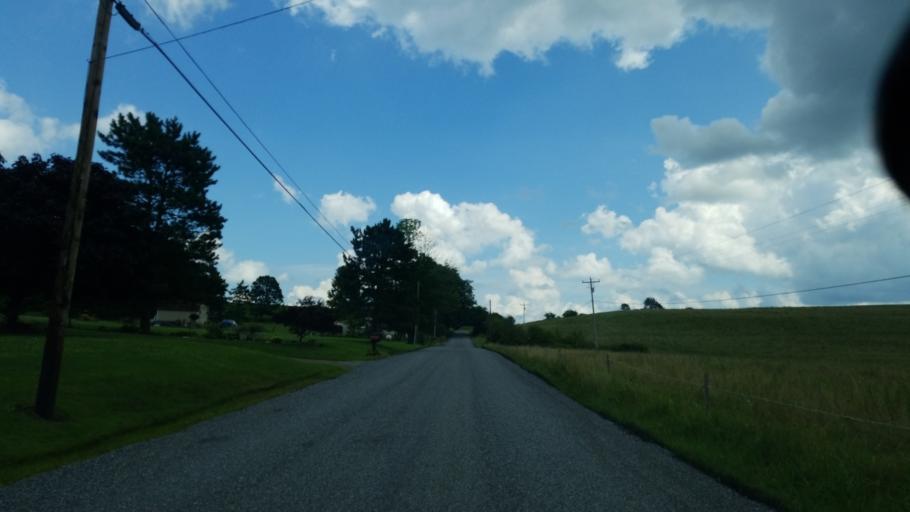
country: US
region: Pennsylvania
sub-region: Jefferson County
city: Brookville
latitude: 41.2318
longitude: -79.0065
